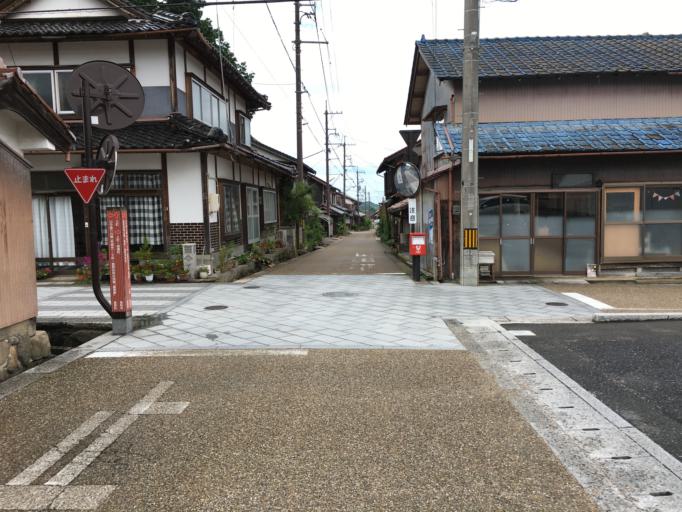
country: JP
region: Tottori
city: Tottori
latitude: 35.4619
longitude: 134.0644
